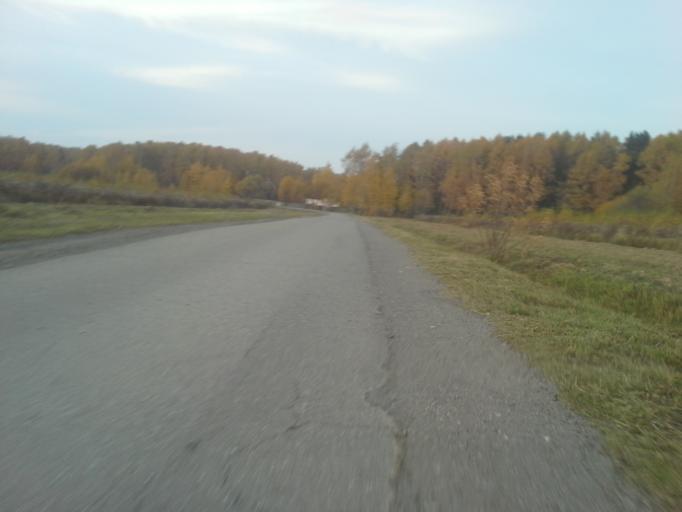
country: RU
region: Moskovskaya
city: Dubrovitsy
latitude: 55.4983
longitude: 37.4327
